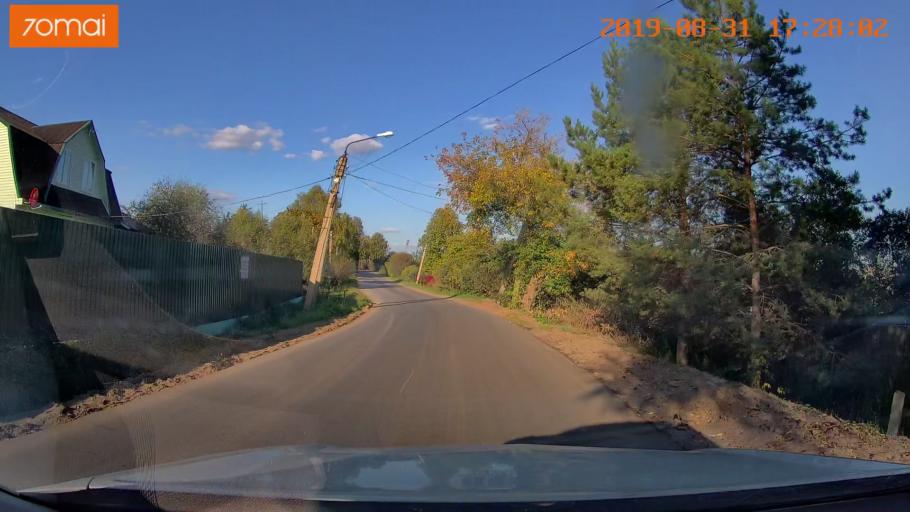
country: RU
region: Kaluga
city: Detchino
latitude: 54.8103
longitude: 36.3135
